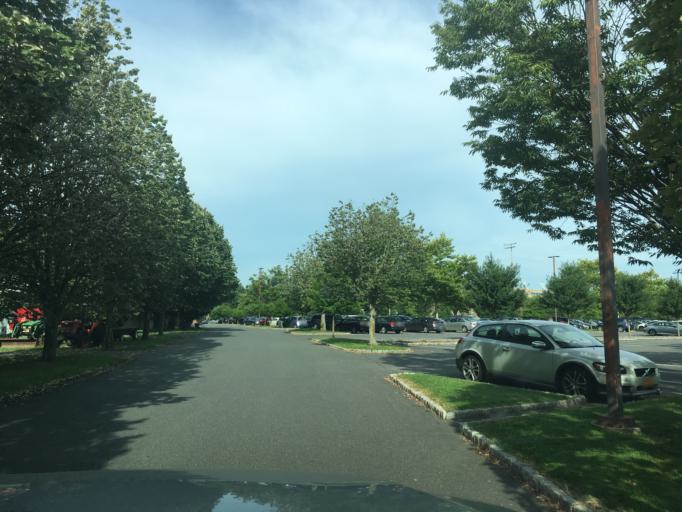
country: US
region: New Jersey
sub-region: Mercer County
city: Princeton
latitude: 40.3446
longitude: -74.6448
